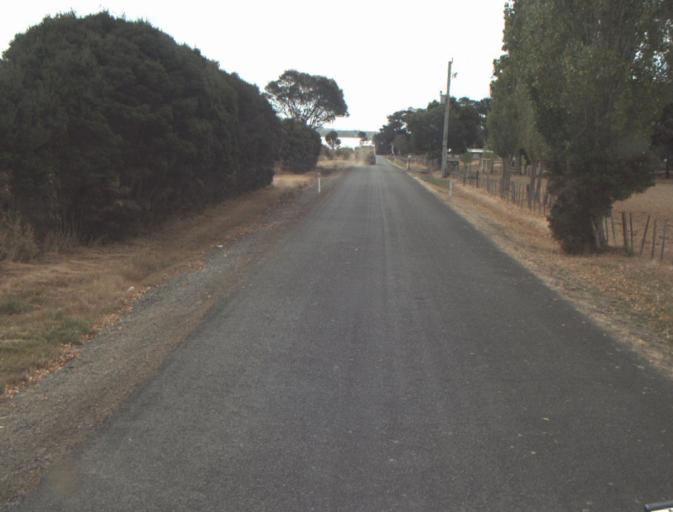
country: AU
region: Tasmania
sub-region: Launceston
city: Mayfield
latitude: -41.2884
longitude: 147.0010
